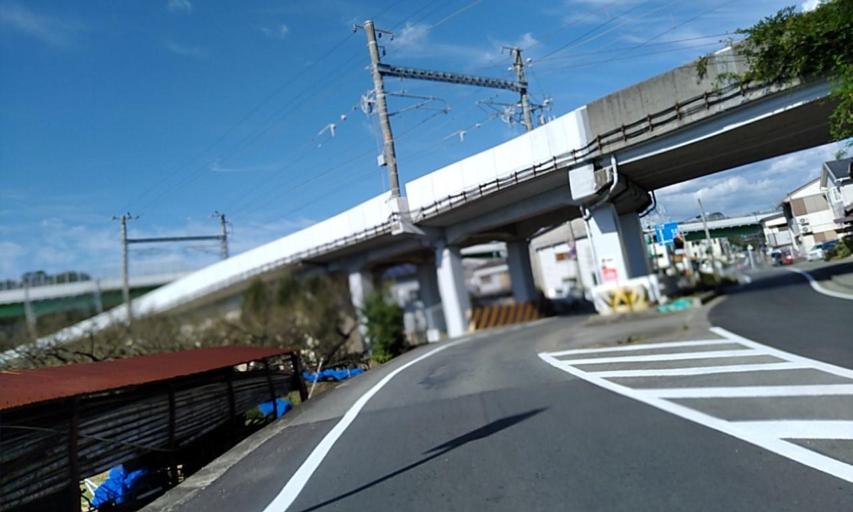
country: JP
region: Wakayama
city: Tanabe
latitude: 33.7502
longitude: 135.3522
